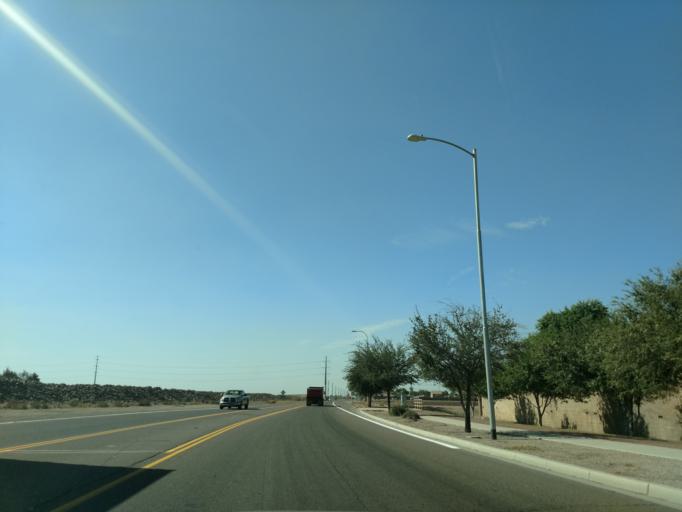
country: US
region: Arizona
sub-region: Maricopa County
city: Laveen
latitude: 33.4080
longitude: -112.1813
